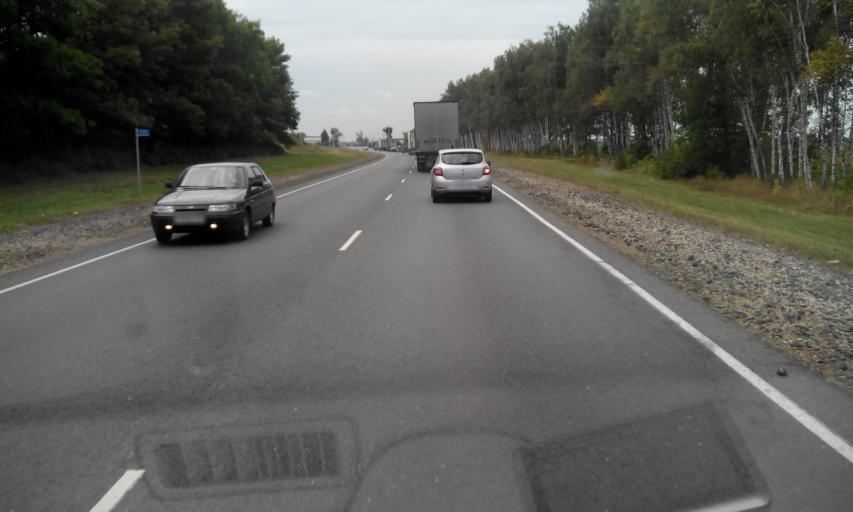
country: RU
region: Penza
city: Poselki
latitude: 53.1048
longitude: 46.4388
